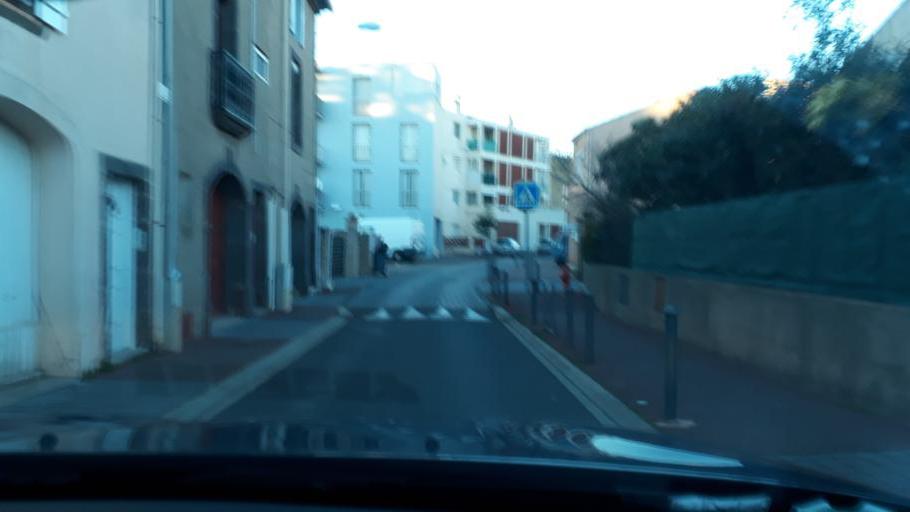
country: FR
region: Languedoc-Roussillon
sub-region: Departement de l'Herault
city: Agde
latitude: 43.3086
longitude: 3.4692
